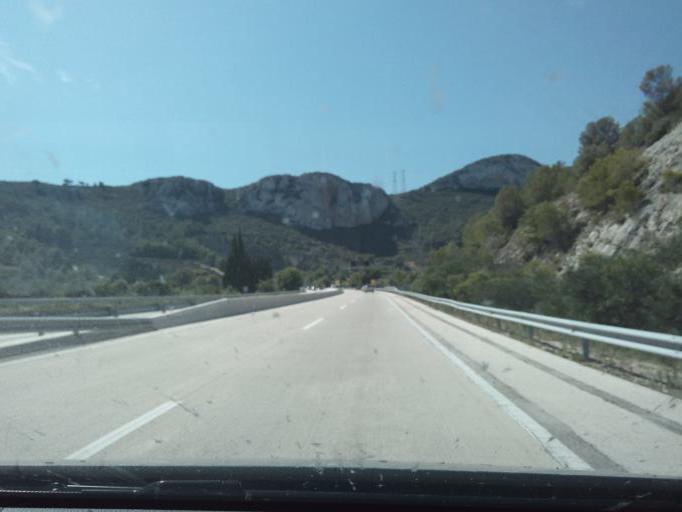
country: ES
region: Valencia
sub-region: Provincia de Valencia
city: Xeresa
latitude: 39.0090
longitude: -0.2240
